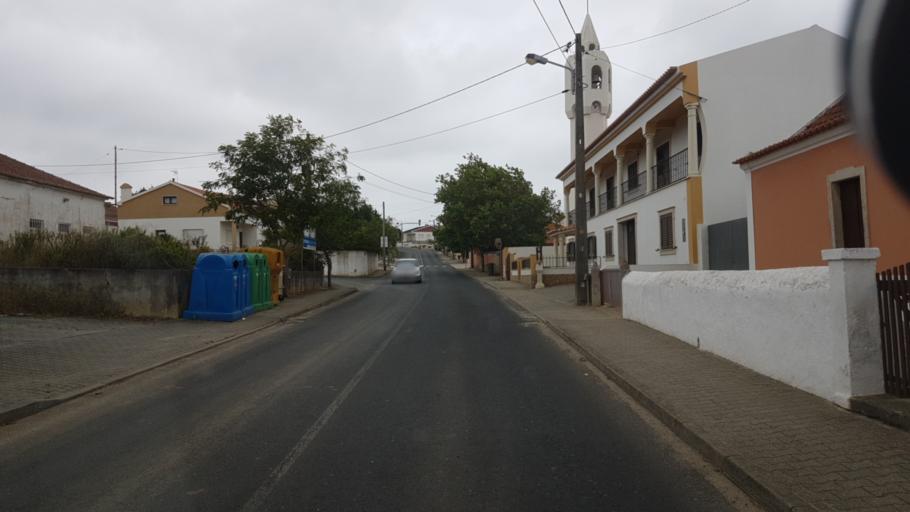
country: PT
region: Lisbon
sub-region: Lourinha
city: Lourinha
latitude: 39.2213
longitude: -9.3175
